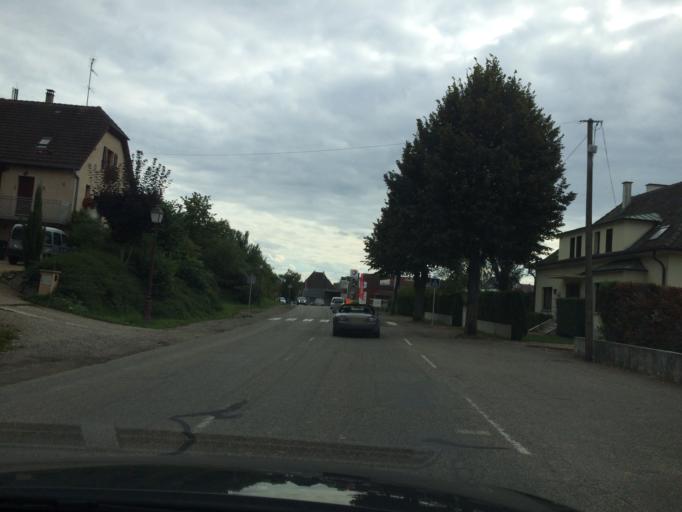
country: FR
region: Alsace
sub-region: Departement du Haut-Rhin
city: Bennwihr
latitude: 48.1557
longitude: 7.3200
